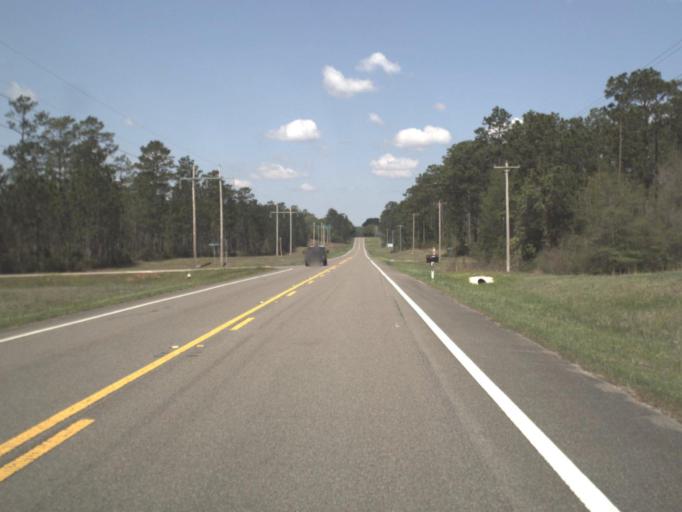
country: US
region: Florida
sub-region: Santa Rosa County
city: Point Baker
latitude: 30.8879
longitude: -86.9709
